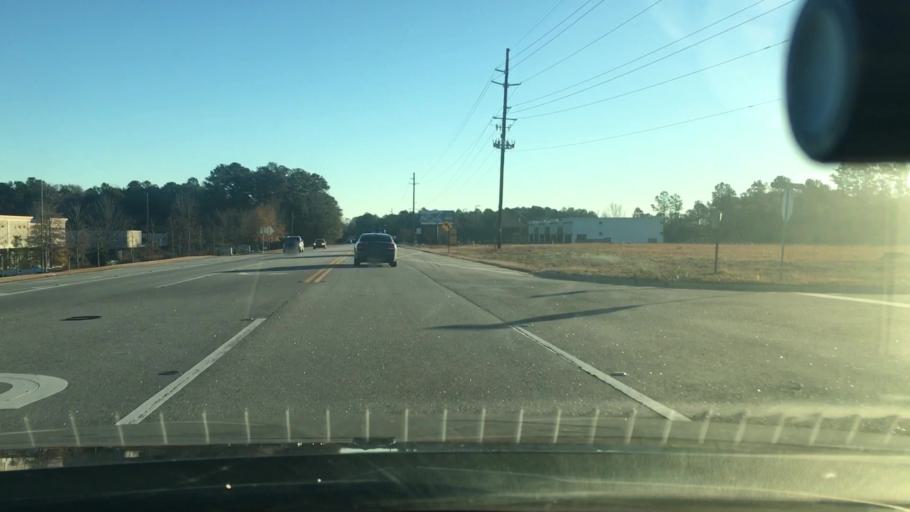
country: US
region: Georgia
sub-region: Coweta County
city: Senoia
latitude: 33.2934
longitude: -84.5748
